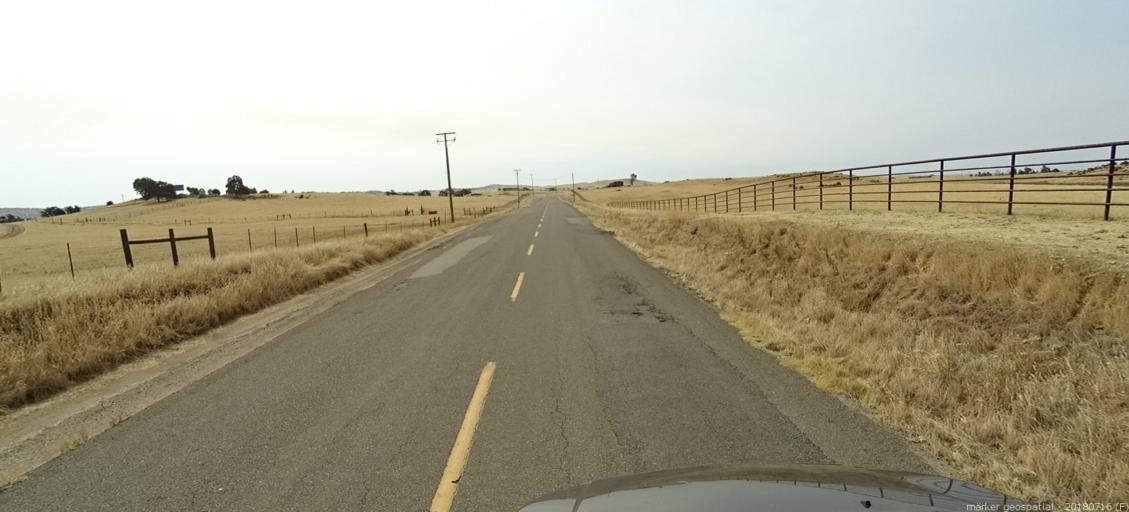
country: US
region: California
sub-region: Madera County
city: Bonadelle Ranchos-Madera Ranchos
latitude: 37.1114
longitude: -119.9138
